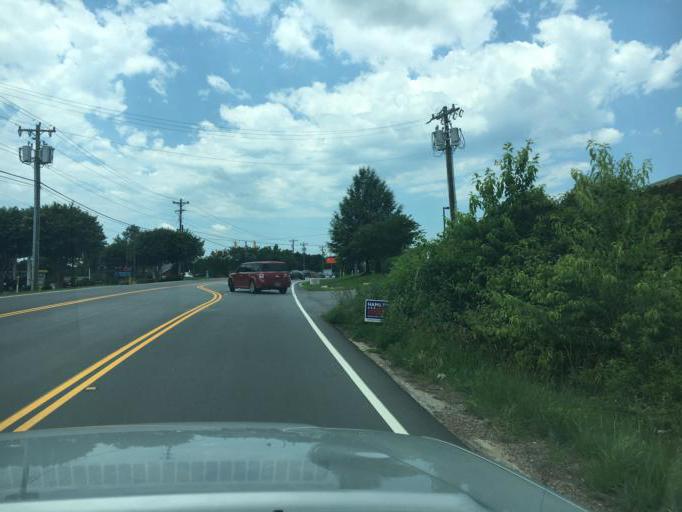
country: US
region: South Carolina
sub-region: Greenville County
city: Taylors
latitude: 34.8716
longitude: -82.2529
